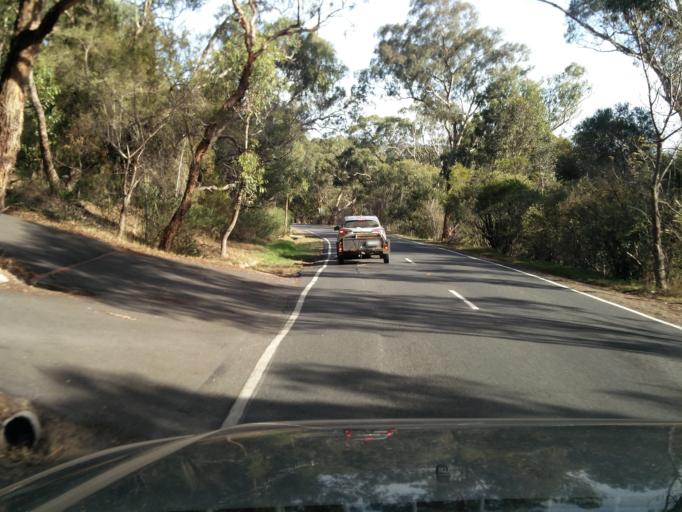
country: AU
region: Victoria
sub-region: Nillumbik
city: Eltham
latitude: -37.7258
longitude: 145.1531
